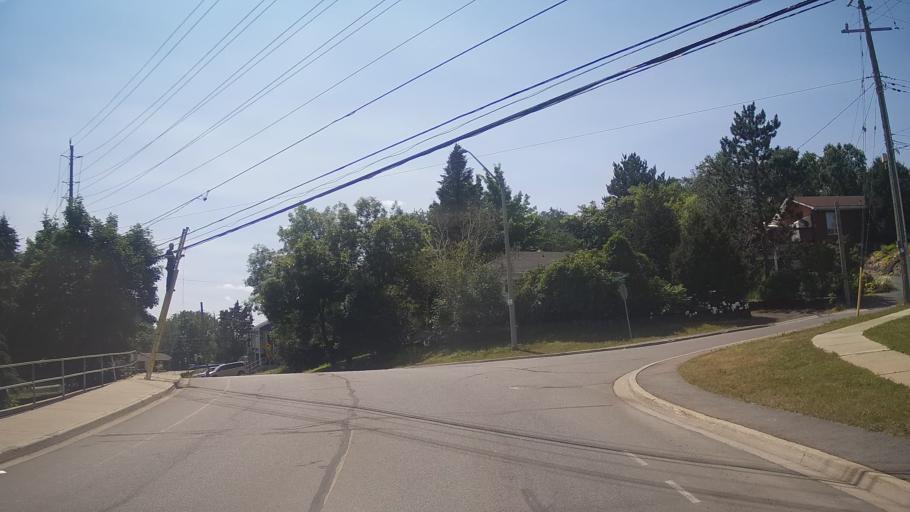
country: CA
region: Ontario
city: Greater Sudbury
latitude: 46.4609
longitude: -81.0145
